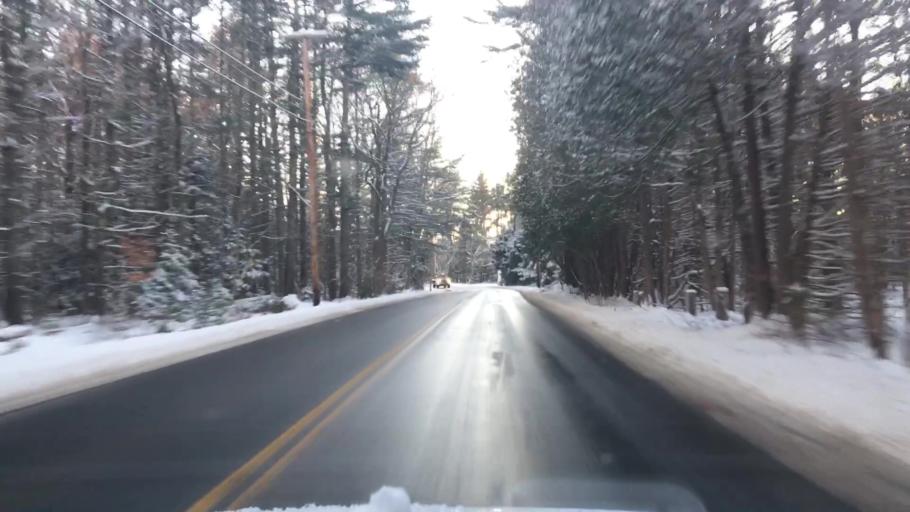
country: US
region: Maine
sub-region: Cumberland County
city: Brunswick
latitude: 43.9530
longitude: -69.9299
